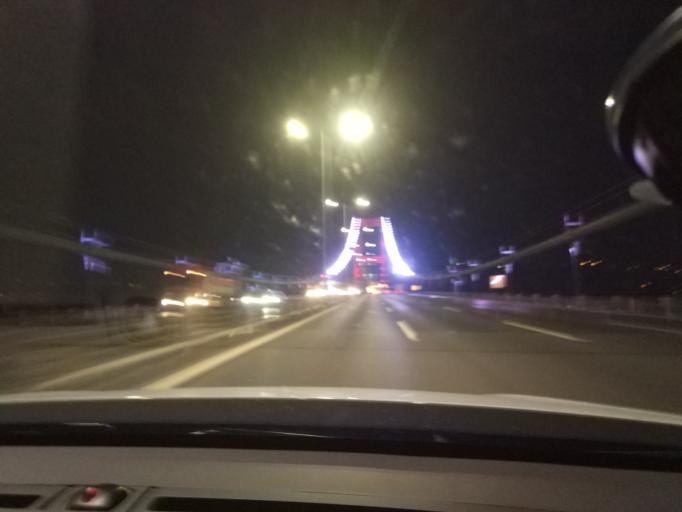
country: TR
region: Istanbul
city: UEskuedar
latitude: 41.0912
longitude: 29.0602
